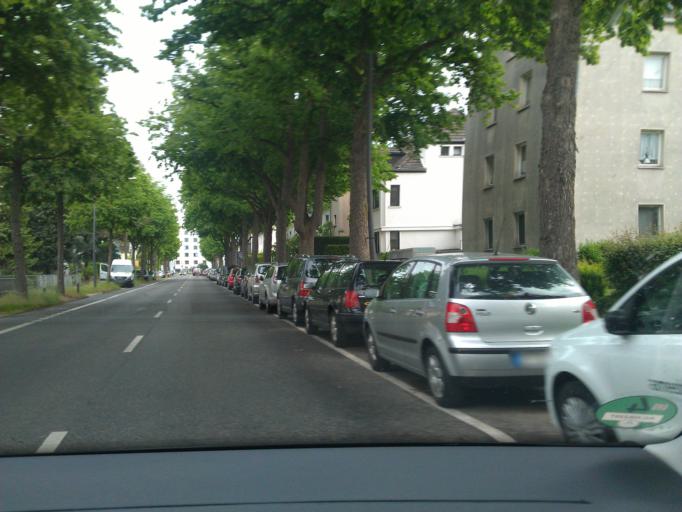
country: DE
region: North Rhine-Westphalia
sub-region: Regierungsbezirk Koln
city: Aachen
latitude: 50.7605
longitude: 6.0986
